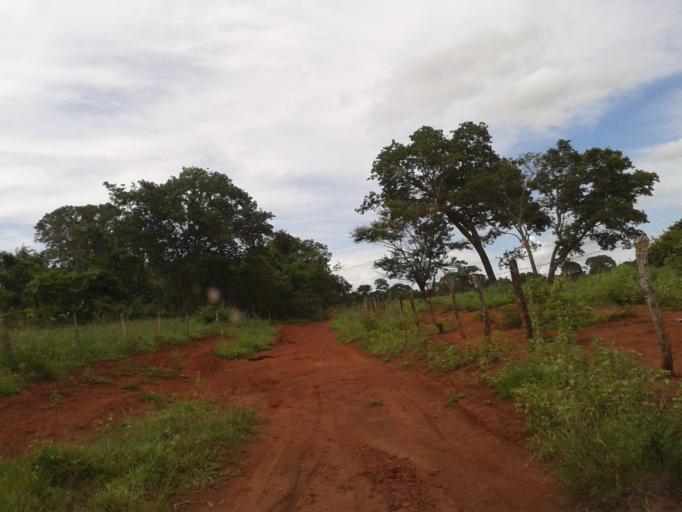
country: BR
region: Minas Gerais
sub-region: Santa Vitoria
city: Santa Vitoria
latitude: -18.7964
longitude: -49.8506
